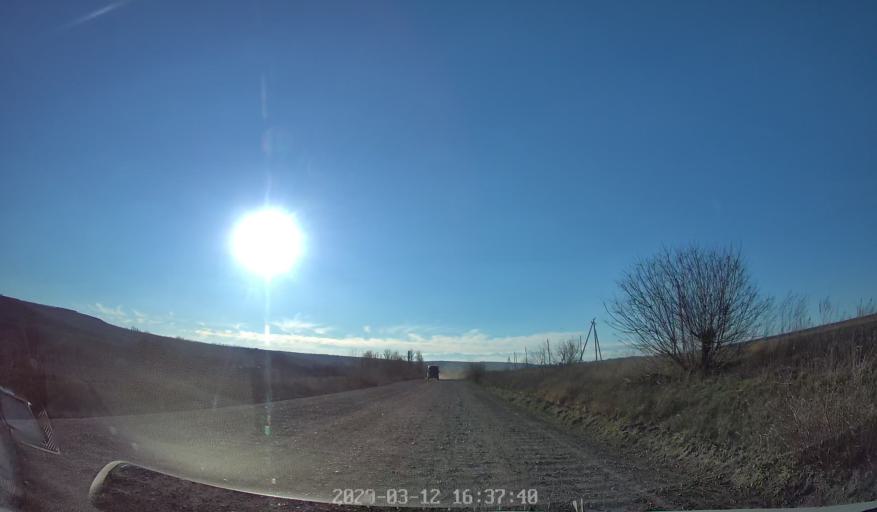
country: MD
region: Anenii Noi
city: Anenii Noi
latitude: 46.8154
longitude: 29.1862
